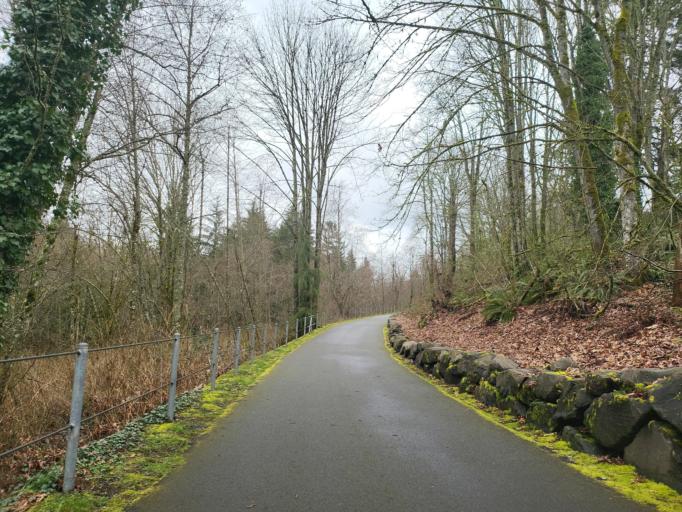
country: US
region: Washington
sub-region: King County
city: East Hill-Meridian
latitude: 47.4228
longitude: -122.1694
